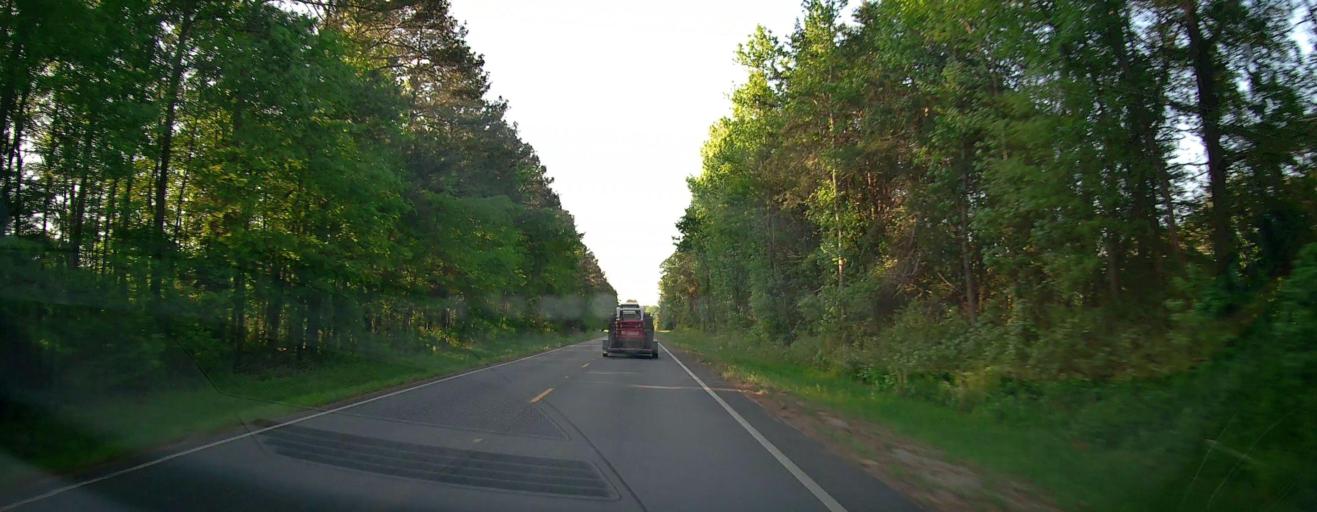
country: US
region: Georgia
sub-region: Putnam County
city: Eatonton
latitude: 33.3454
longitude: -83.5137
